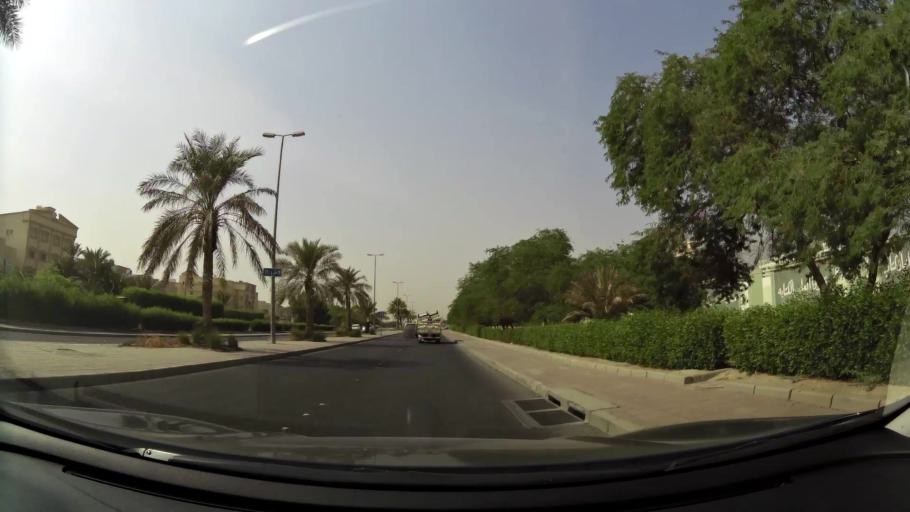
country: KW
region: Al Asimah
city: Ar Rabiyah
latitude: 29.3029
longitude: 47.8681
